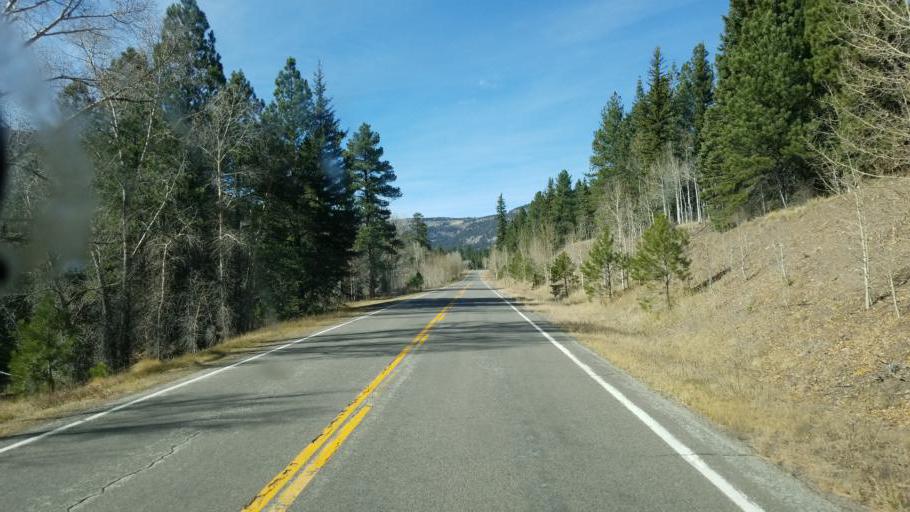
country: US
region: Colorado
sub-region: Conejos County
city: Conejos
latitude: 37.1041
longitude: -106.3120
